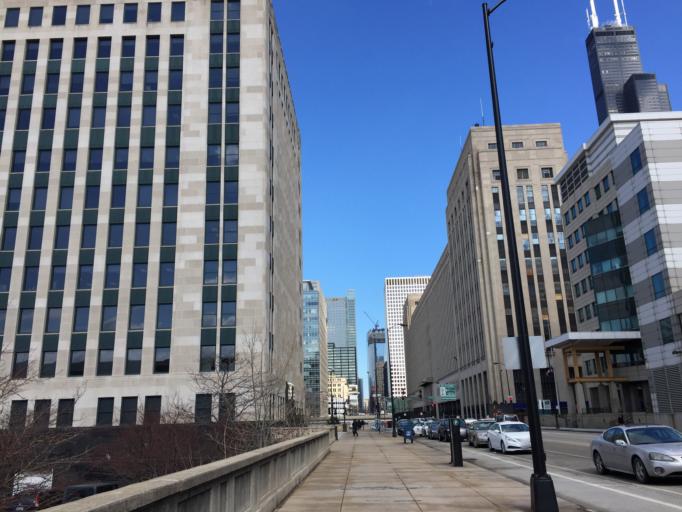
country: US
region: Illinois
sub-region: Cook County
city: Chicago
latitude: 41.8733
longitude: -87.6395
